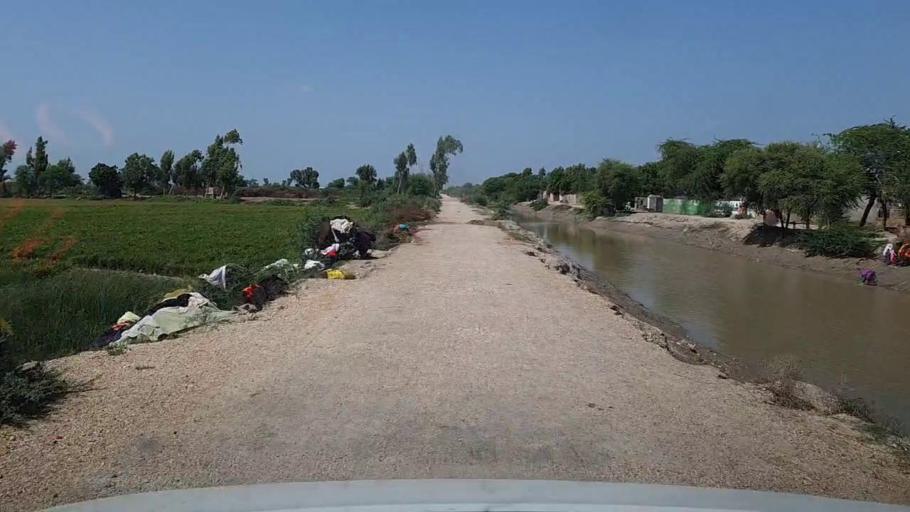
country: PK
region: Sindh
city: Kario
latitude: 24.6538
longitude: 68.5527
